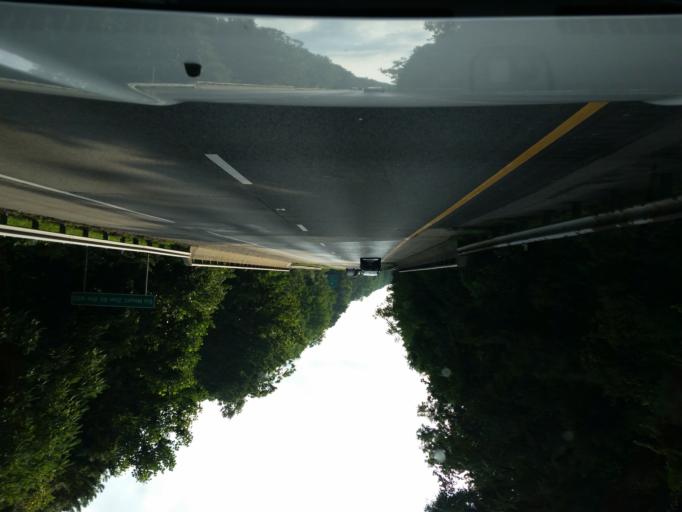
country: US
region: Virginia
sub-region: King William County
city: West Point
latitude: 37.4140
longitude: -76.8006
